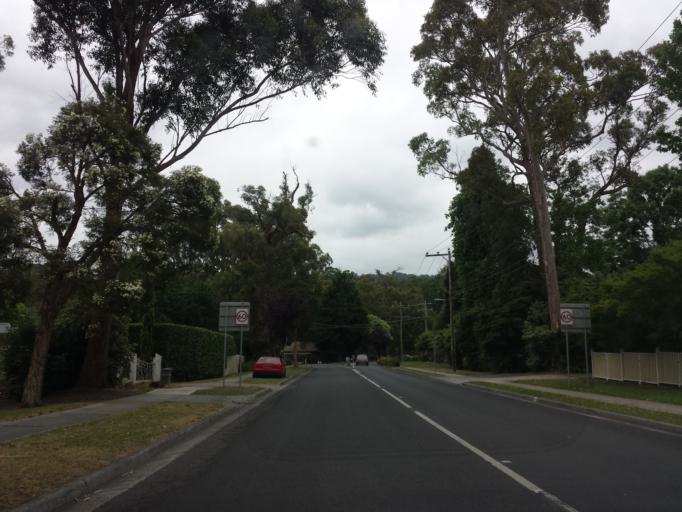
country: AU
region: Victoria
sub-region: Yarra Ranges
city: Tremont
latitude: -37.9119
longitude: 145.3272
